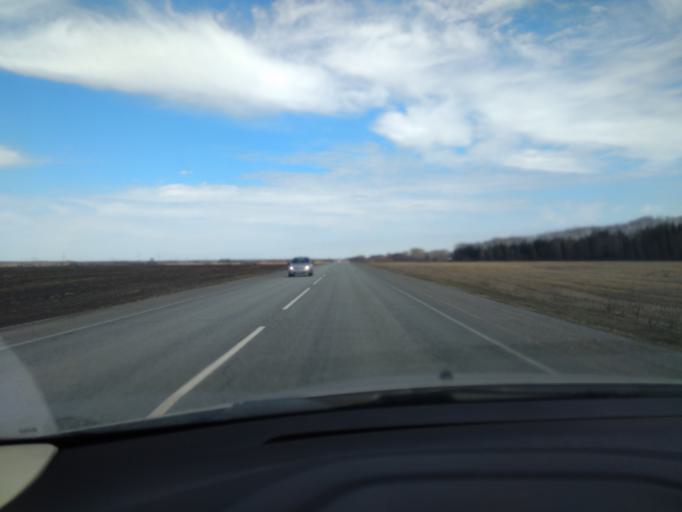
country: RU
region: Sverdlovsk
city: Pyshma
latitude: 57.0106
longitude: 63.3522
